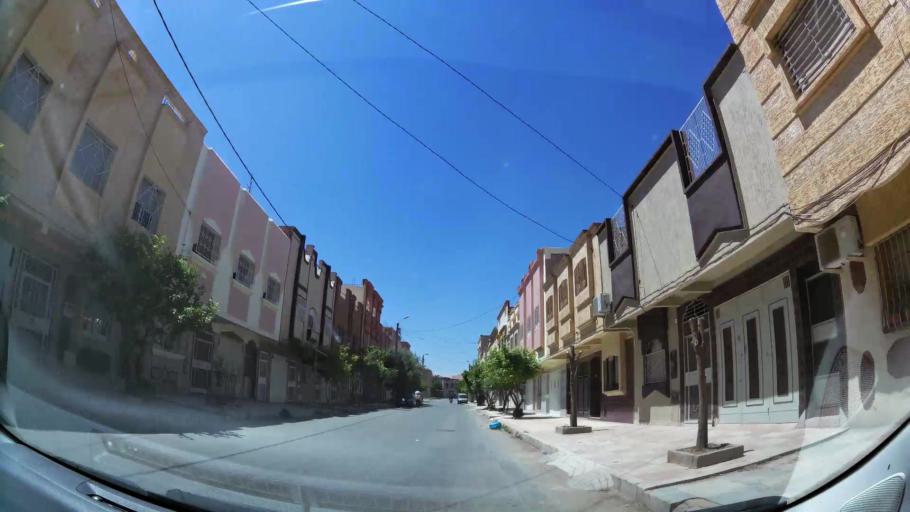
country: MA
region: Oriental
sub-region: Oujda-Angad
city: Oujda
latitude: 34.6704
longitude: -1.8892
